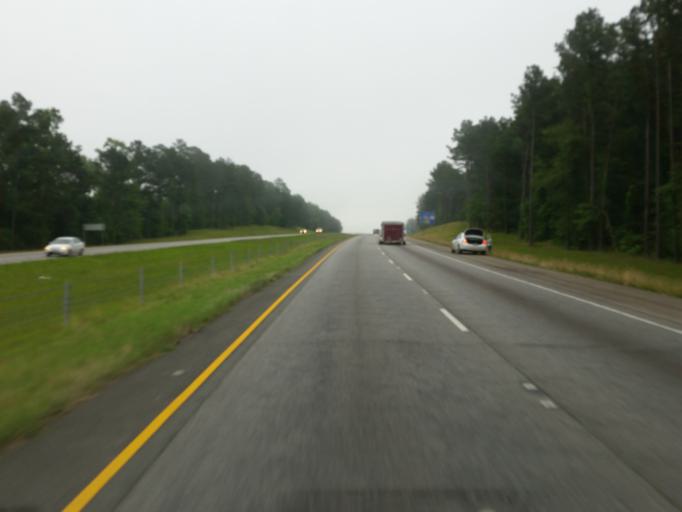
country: US
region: Louisiana
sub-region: Webster Parish
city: Minden
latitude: 32.5931
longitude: -93.3075
